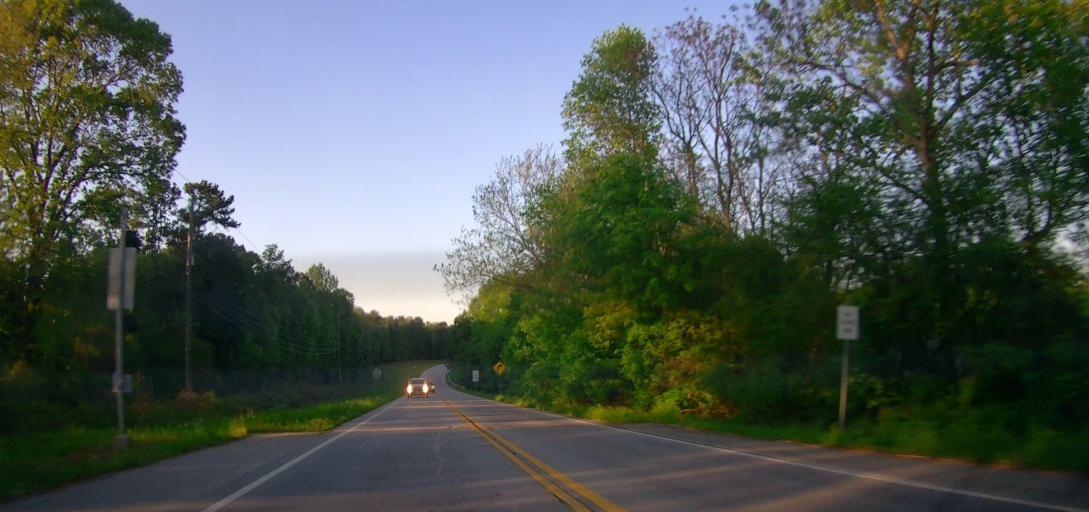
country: US
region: Georgia
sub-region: Newton County
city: Oakwood
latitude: 33.5422
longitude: -83.9491
